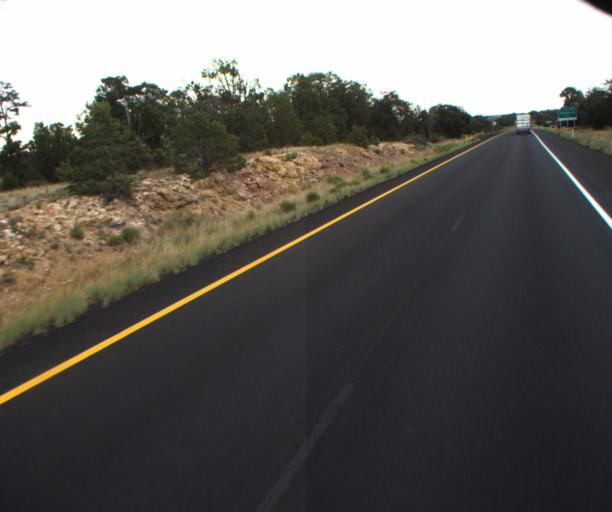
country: US
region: Arizona
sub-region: Coconino County
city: Flagstaff
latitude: 35.2053
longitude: -111.4977
